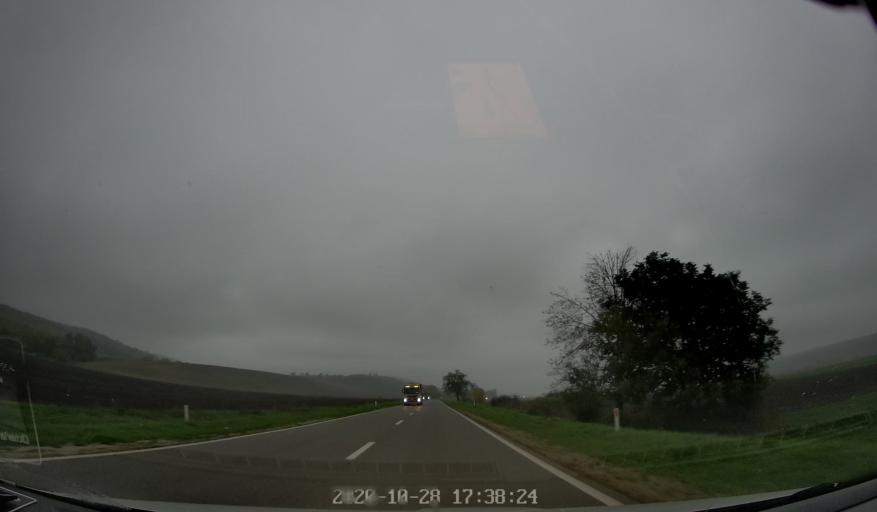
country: MD
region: Hincesti
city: Hincesti
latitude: 46.7829
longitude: 28.6257
